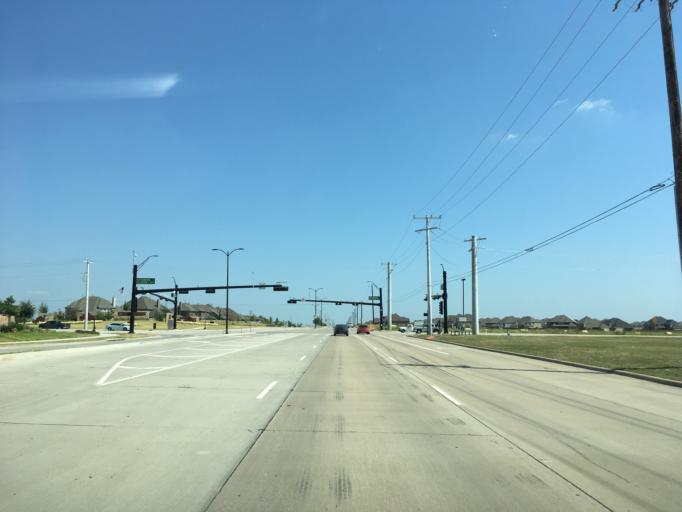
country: US
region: Texas
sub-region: Collin County
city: Prosper
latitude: 33.1881
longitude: -96.7678
